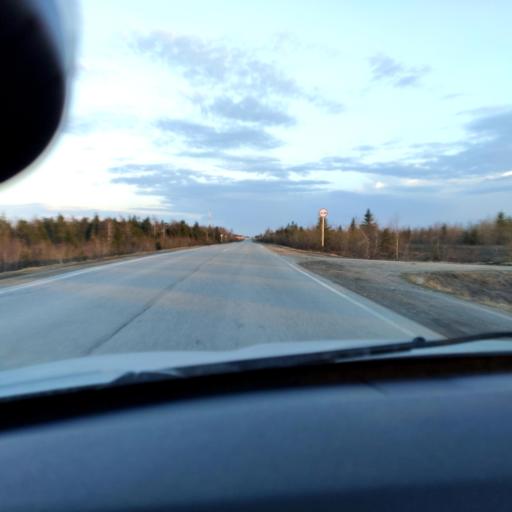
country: RU
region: Perm
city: Gremyachinsk
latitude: 58.5813
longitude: 57.7707
